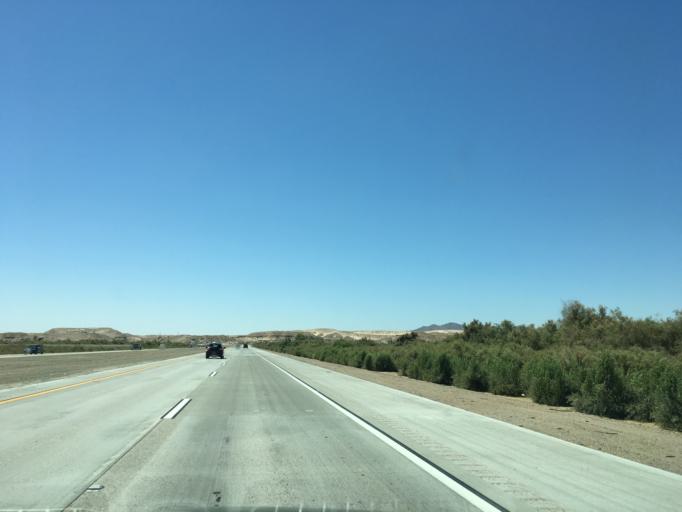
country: MX
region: Baja California
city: Los Algodones
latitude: 32.7428
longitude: -114.6874
